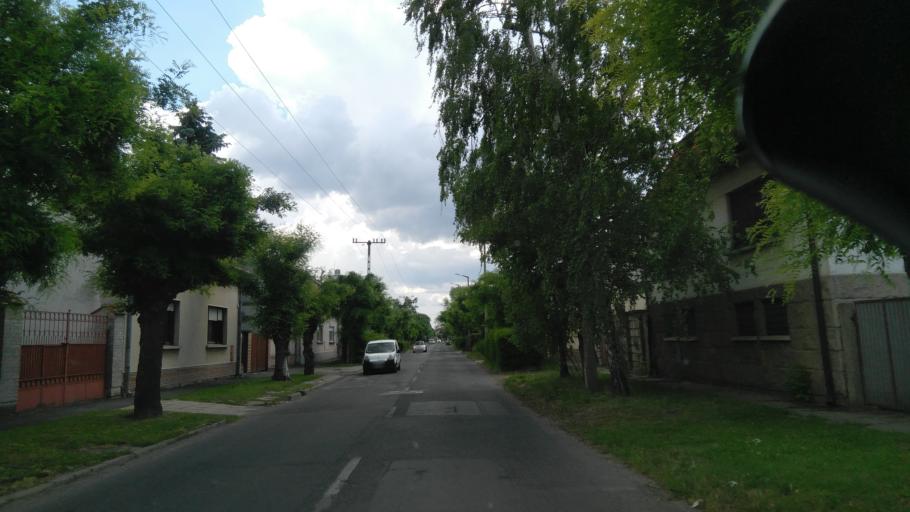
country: HU
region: Bekes
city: Gyula
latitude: 46.6530
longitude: 21.2694
